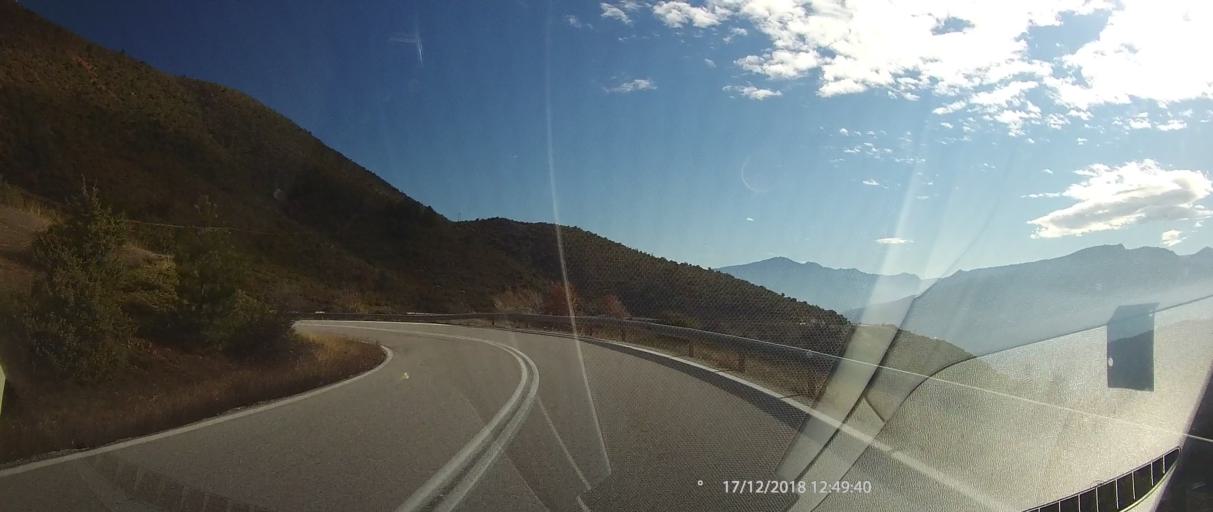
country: GR
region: Thessaly
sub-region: Trikala
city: Kastraki
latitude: 39.7773
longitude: 21.4481
